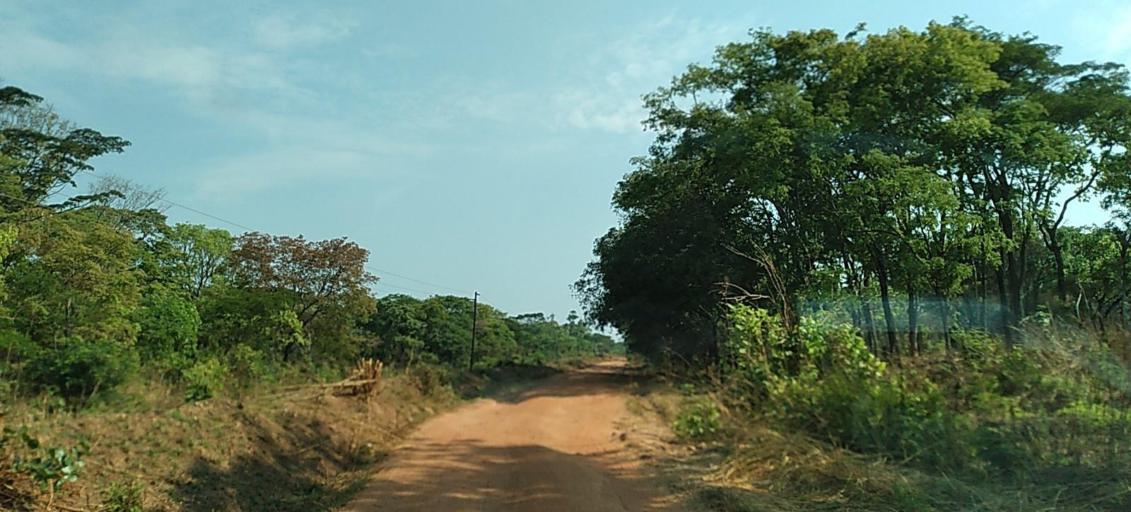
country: ZM
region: Copperbelt
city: Kalulushi
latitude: -13.0075
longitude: 27.8131
